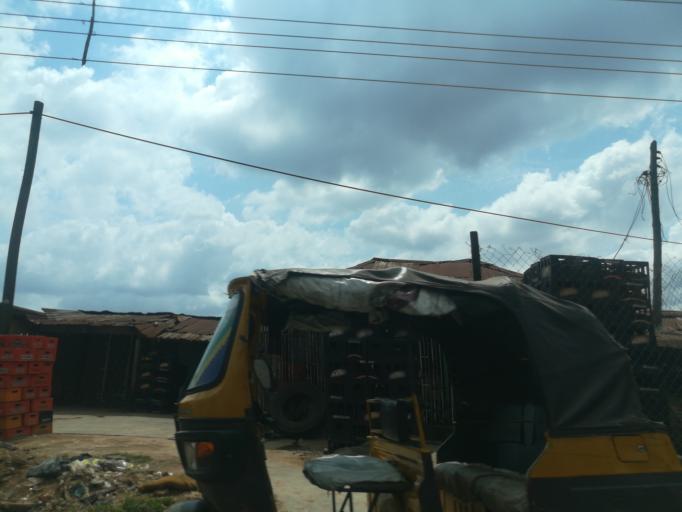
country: NG
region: Oyo
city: Ibadan
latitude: 7.3920
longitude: 3.9134
